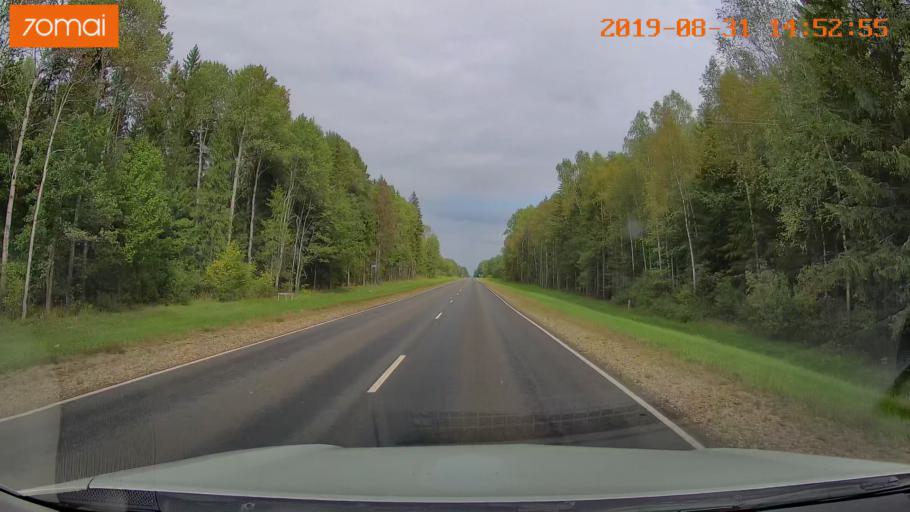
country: RU
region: Kaluga
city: Spas-Demensk
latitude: 54.2795
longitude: 33.8515
